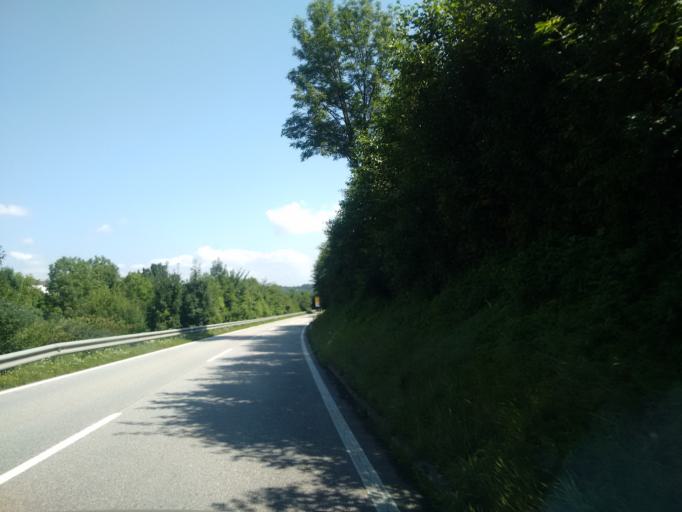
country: AT
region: Upper Austria
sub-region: Politischer Bezirk Kirchdorf an der Krems
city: Kremsmunster
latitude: 48.0471
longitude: 14.1301
